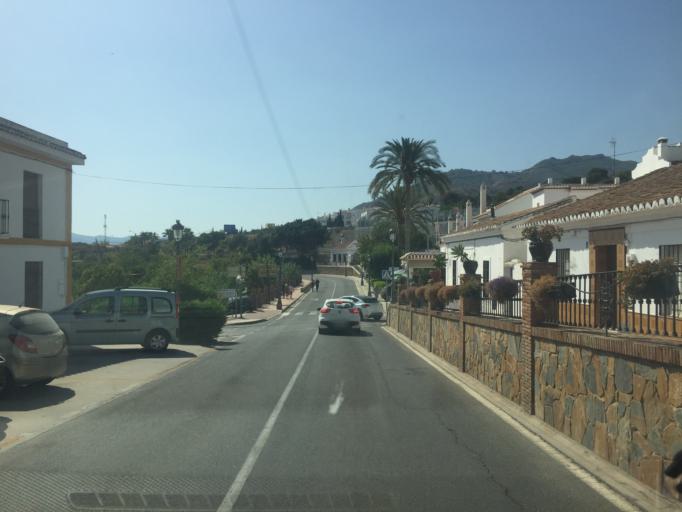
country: ES
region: Andalusia
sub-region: Provincia de Malaga
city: Nerja
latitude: 36.7592
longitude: -3.8438
